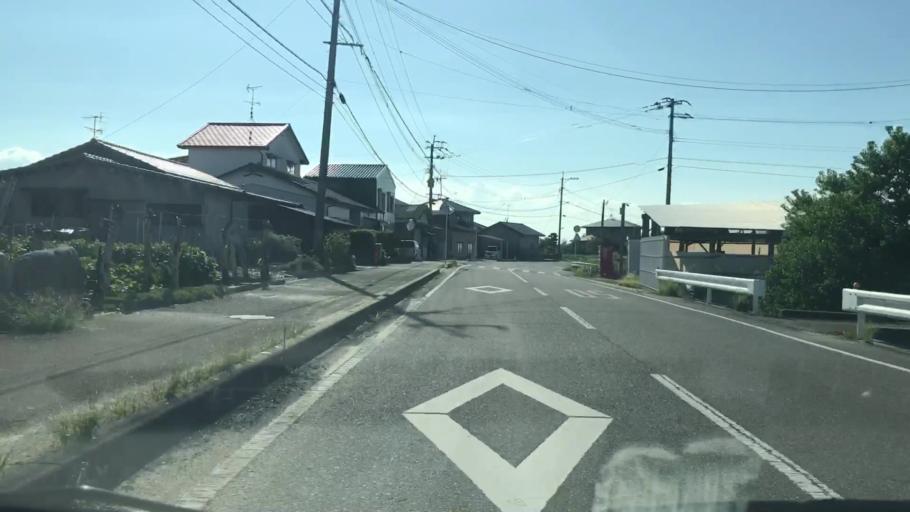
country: JP
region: Saga Prefecture
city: Saga-shi
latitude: 33.1909
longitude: 130.2830
